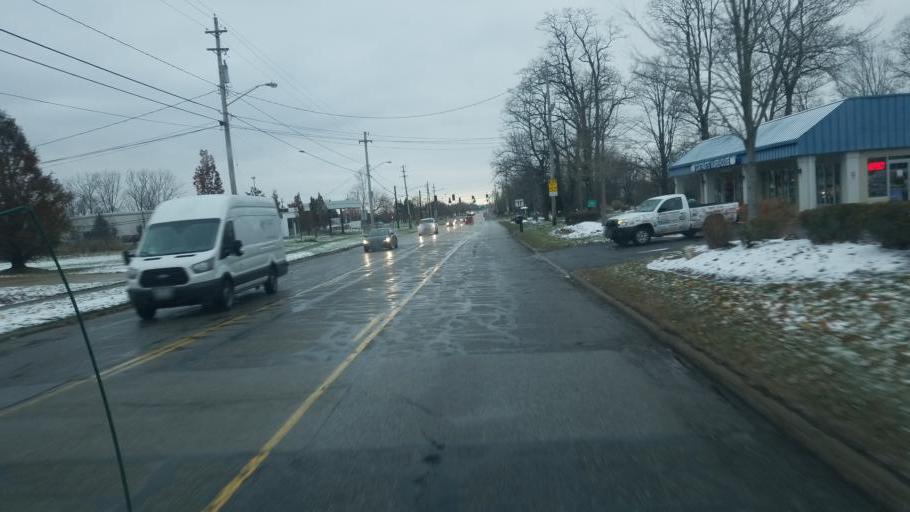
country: US
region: Ohio
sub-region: Cuyahoga County
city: Oakwood
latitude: 41.3642
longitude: -81.5067
